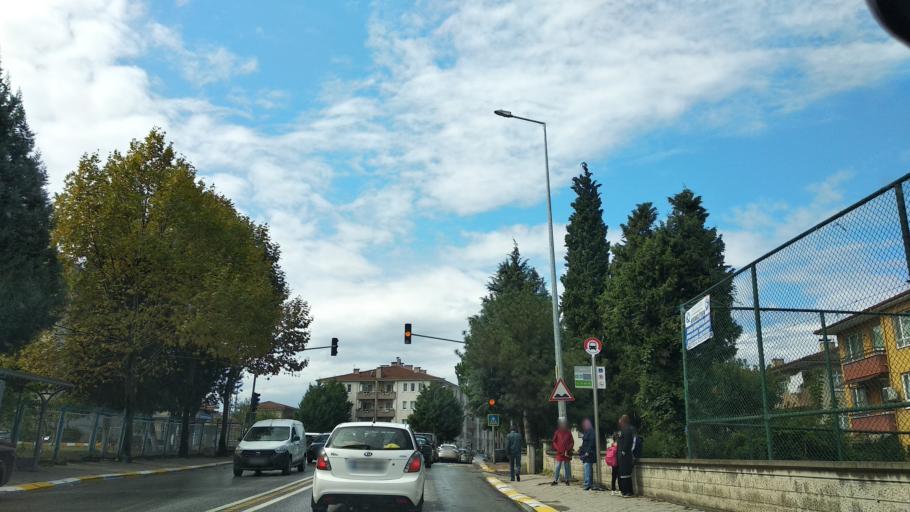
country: TR
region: Sakarya
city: Adapazari
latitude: 40.7580
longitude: 30.3696
